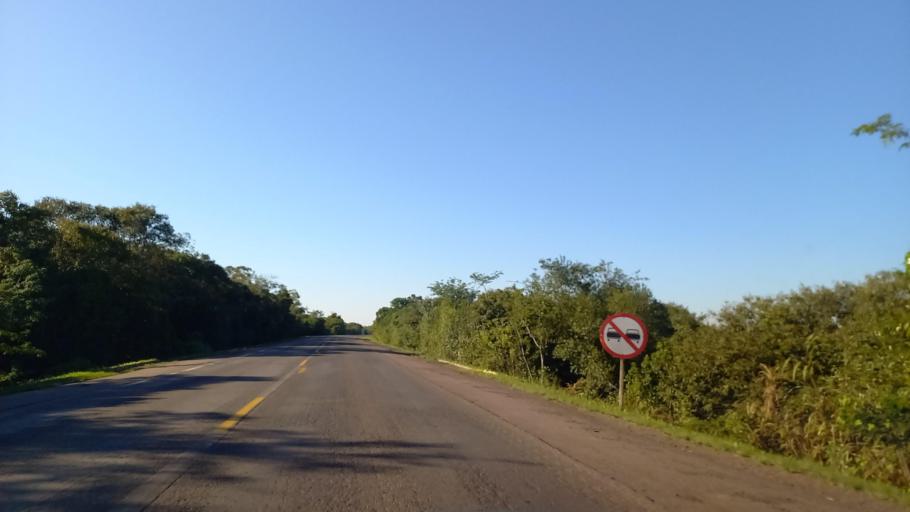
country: BR
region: Rio Grande do Sul
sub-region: Taquari
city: Taquari
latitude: -29.6767
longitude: -52.0124
